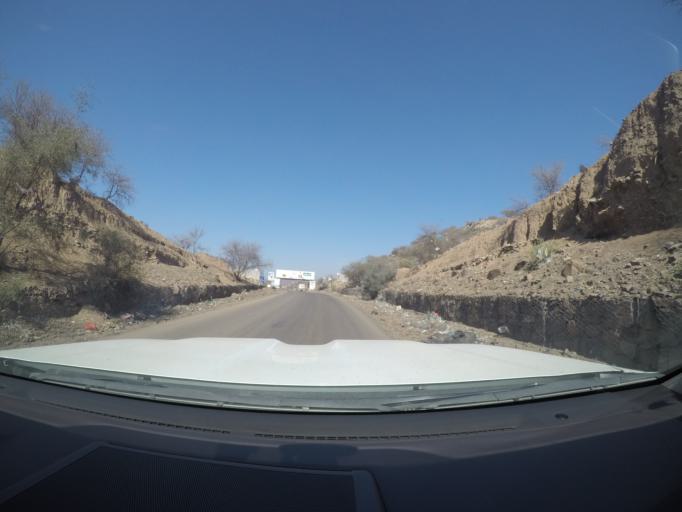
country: YE
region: Ad Dali'
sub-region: Ad Dhale'e
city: Dhalie
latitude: 13.6729
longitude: 44.7658
